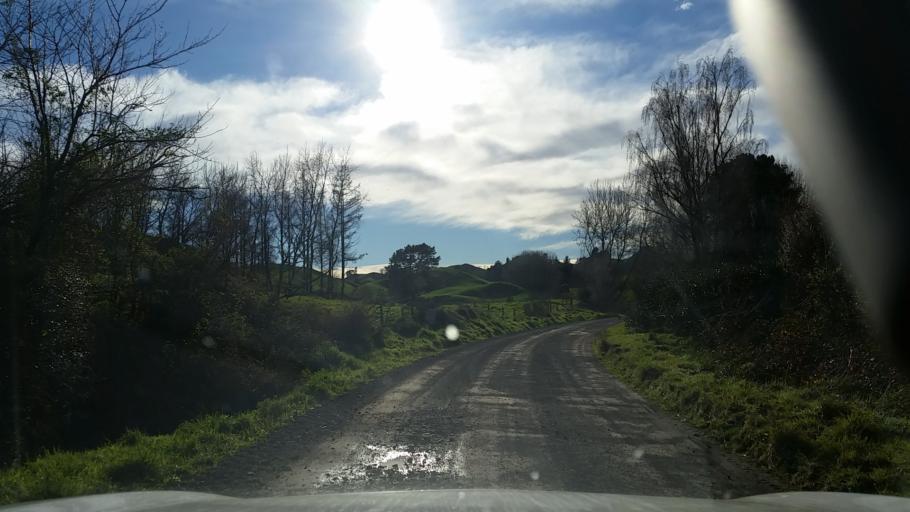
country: NZ
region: Waikato
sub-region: South Waikato District
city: Tokoroa
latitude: -38.3853
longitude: 176.0785
